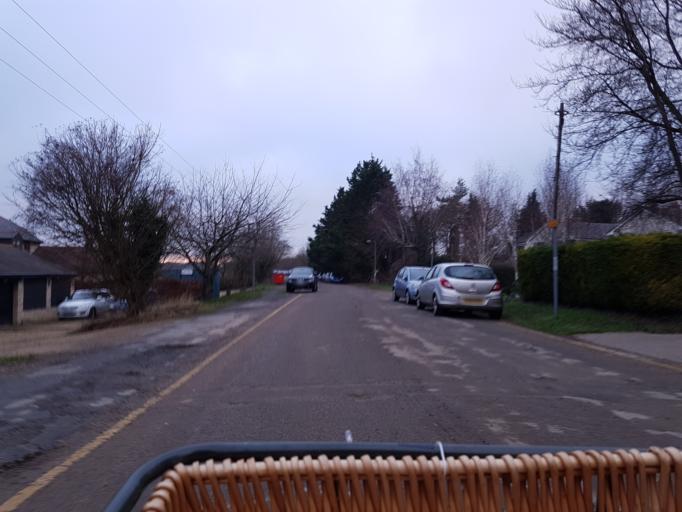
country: GB
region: England
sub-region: Cambridgeshire
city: Duxford
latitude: 52.1035
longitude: 0.1576
